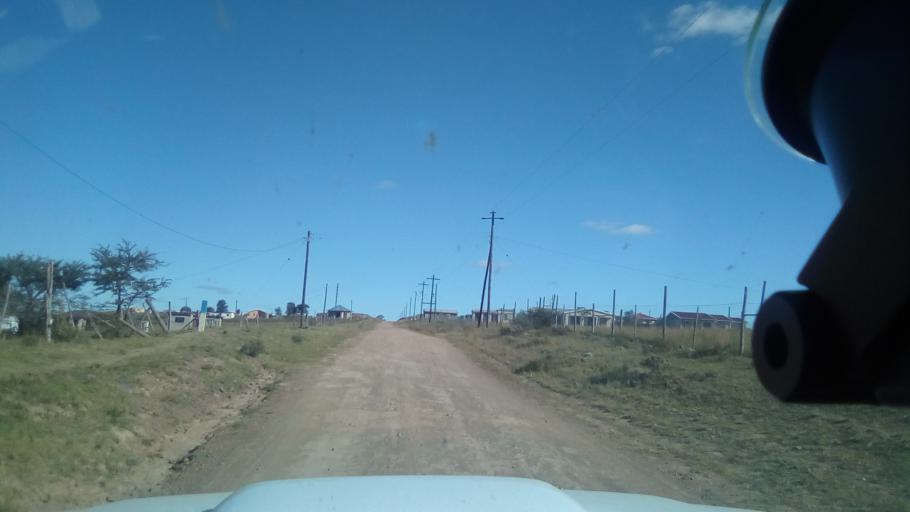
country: ZA
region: Eastern Cape
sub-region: Buffalo City Metropolitan Municipality
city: Bhisho
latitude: -32.7856
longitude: 27.3296
